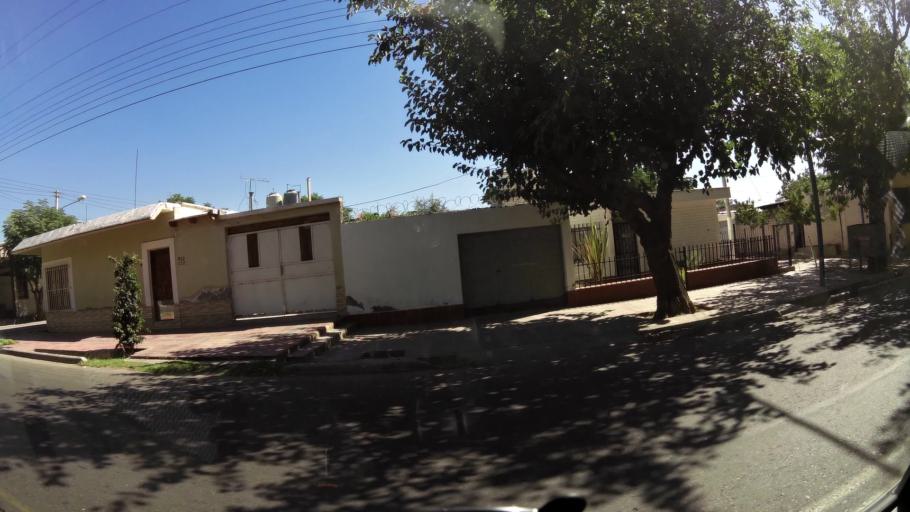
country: AR
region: Mendoza
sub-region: Departamento de Godoy Cruz
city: Godoy Cruz
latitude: -32.9073
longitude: -68.8693
